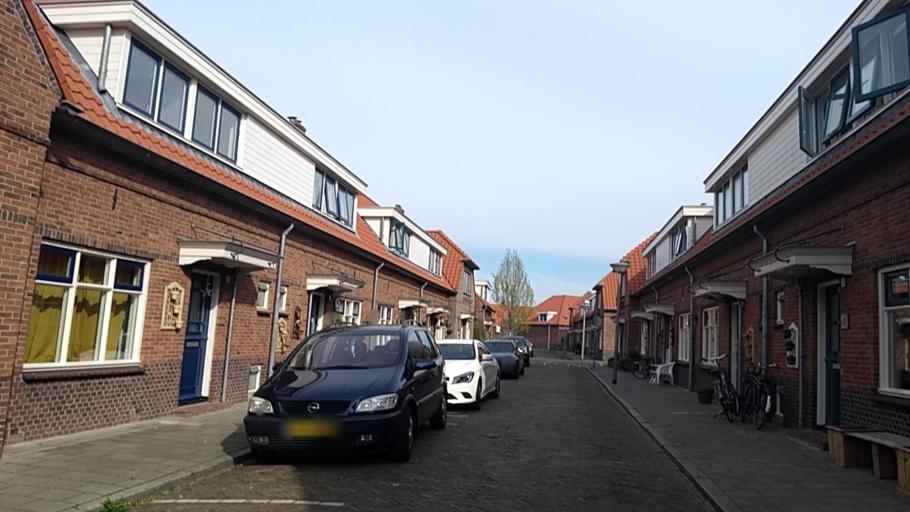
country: NL
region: Overijssel
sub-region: Gemeente Almelo
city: Almelo
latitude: 52.3474
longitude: 6.6523
